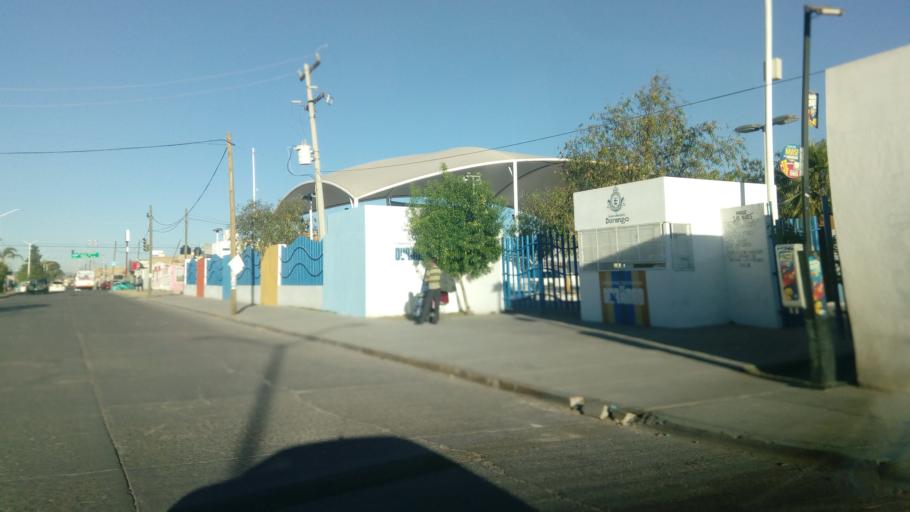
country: MX
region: Durango
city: Victoria de Durango
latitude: 24.0548
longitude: -104.5956
